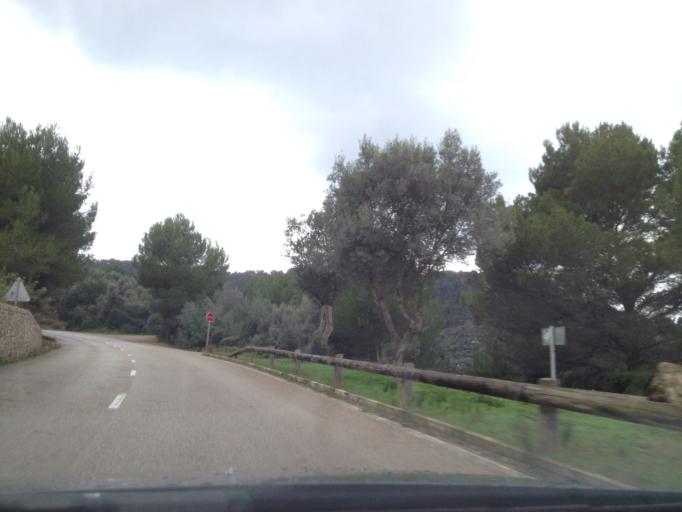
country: ES
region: Balearic Islands
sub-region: Illes Balears
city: Soller
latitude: 39.7745
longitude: 2.6980
